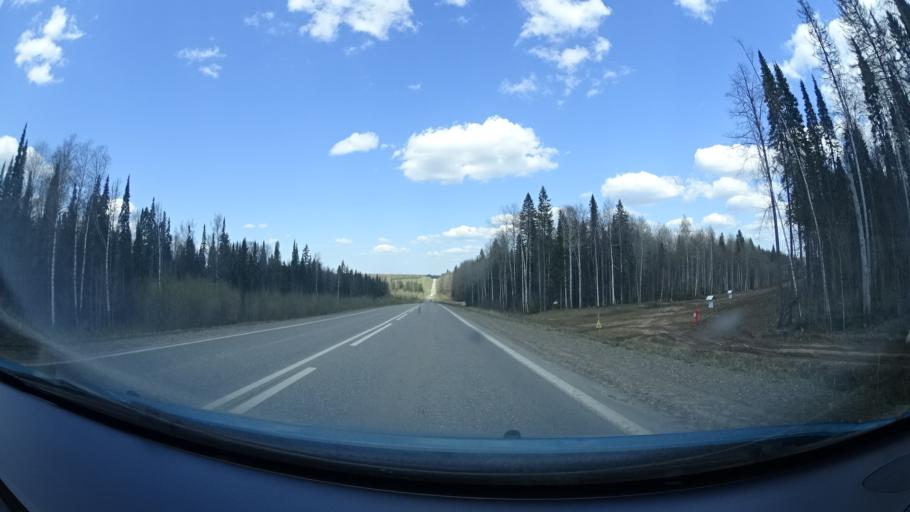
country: RU
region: Perm
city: Osa
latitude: 57.4097
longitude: 55.6232
